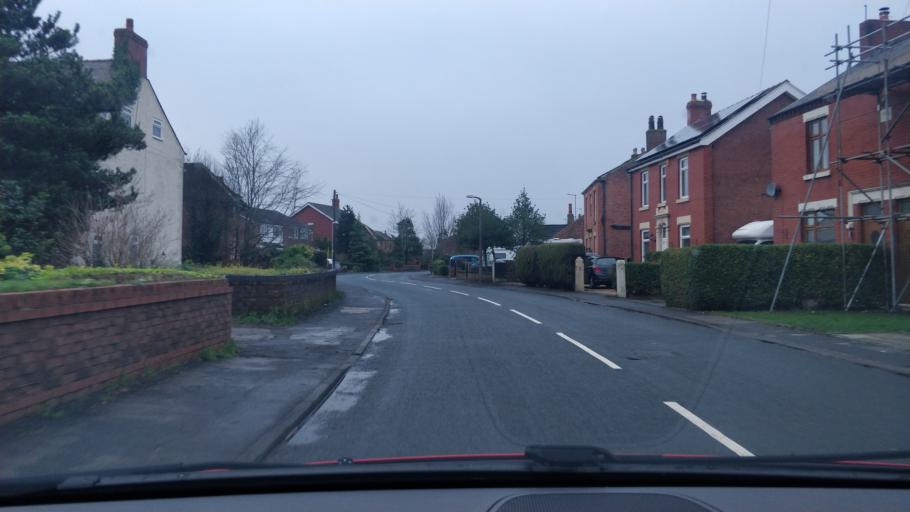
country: GB
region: England
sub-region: Lancashire
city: Tarleton
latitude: 53.7034
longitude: -2.7975
